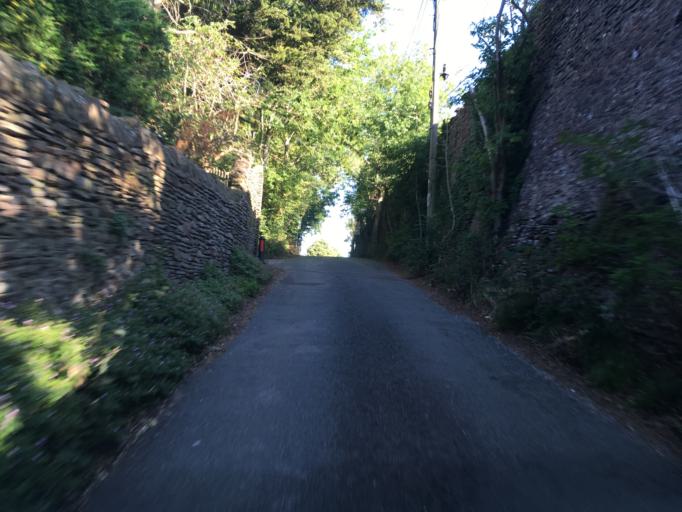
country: GB
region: England
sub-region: South Gloucestershire
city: Winterbourne
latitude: 51.5100
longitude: -2.5093
